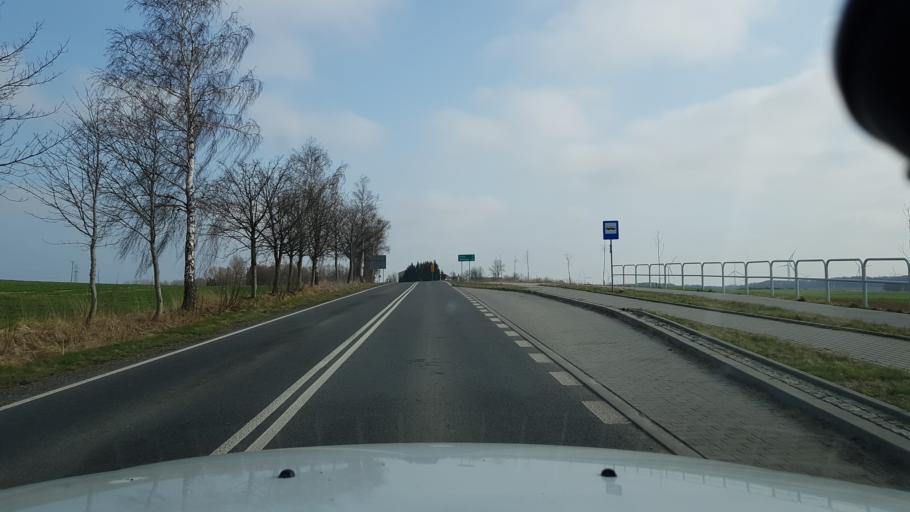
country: PL
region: West Pomeranian Voivodeship
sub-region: Powiat koszalinski
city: Sianow
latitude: 54.2928
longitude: 16.3031
